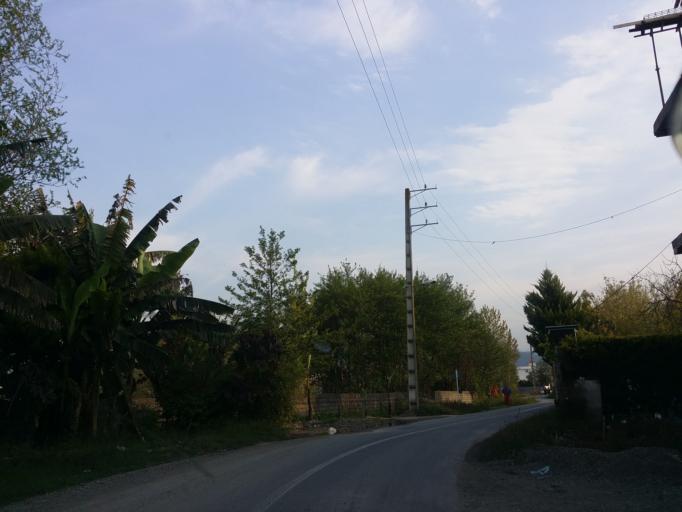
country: IR
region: Mazandaran
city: Chalus
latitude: 36.6839
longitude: 51.3720
